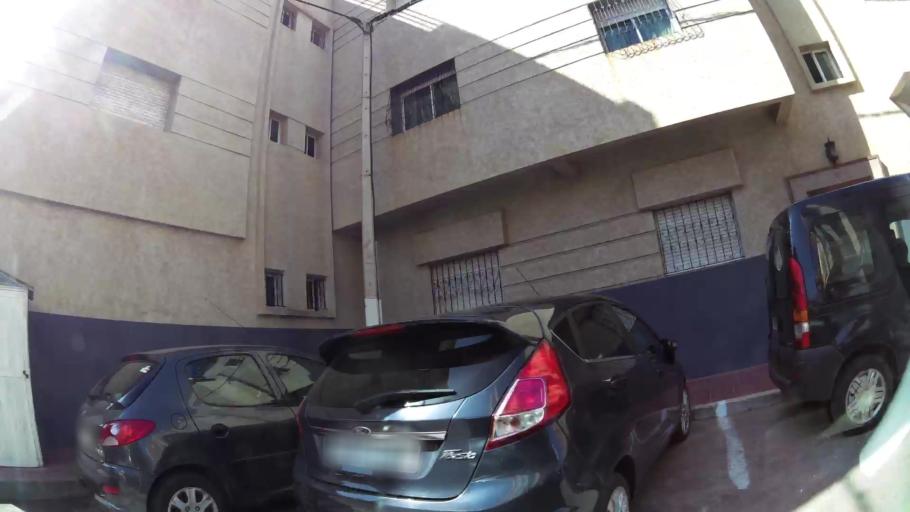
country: MA
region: Rabat-Sale-Zemmour-Zaer
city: Sale
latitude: 34.0652
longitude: -6.8006
